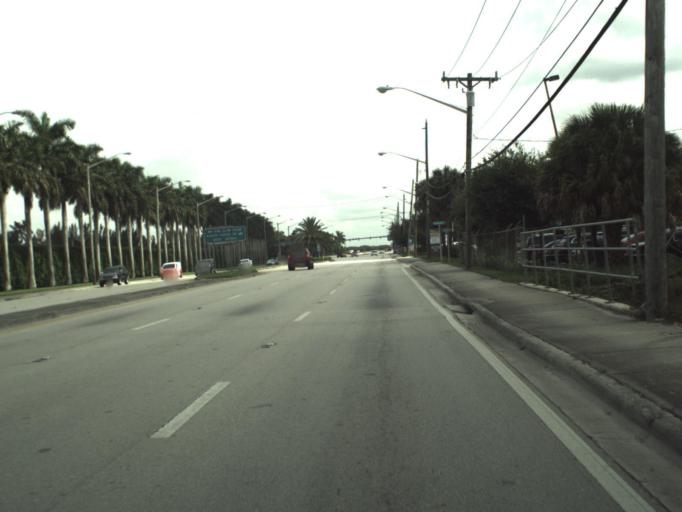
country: US
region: Florida
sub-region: Palm Beach County
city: Lake Clarke Shores
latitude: 26.6691
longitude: -80.0878
